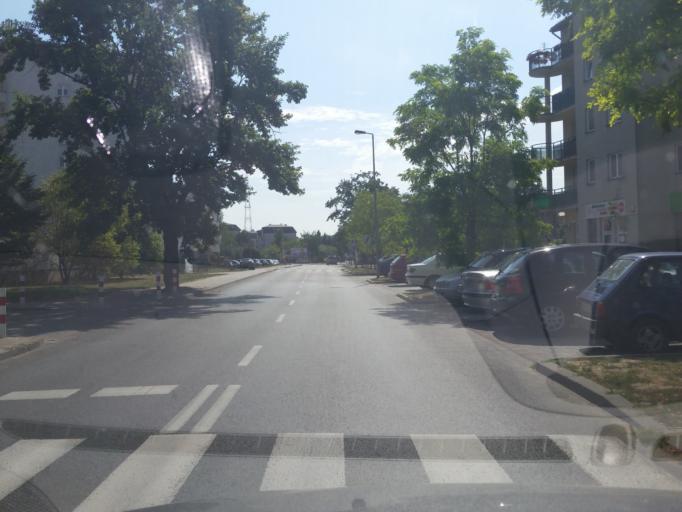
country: PL
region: Masovian Voivodeship
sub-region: Warszawa
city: Bialoleka
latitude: 52.3347
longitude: 20.9368
